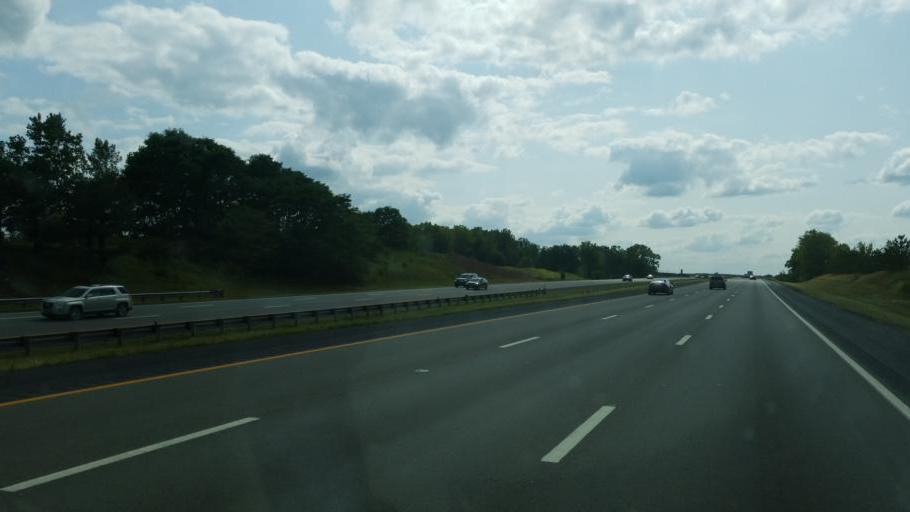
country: US
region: Ohio
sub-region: Medina County
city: Lodi
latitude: 40.9987
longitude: -81.9767
